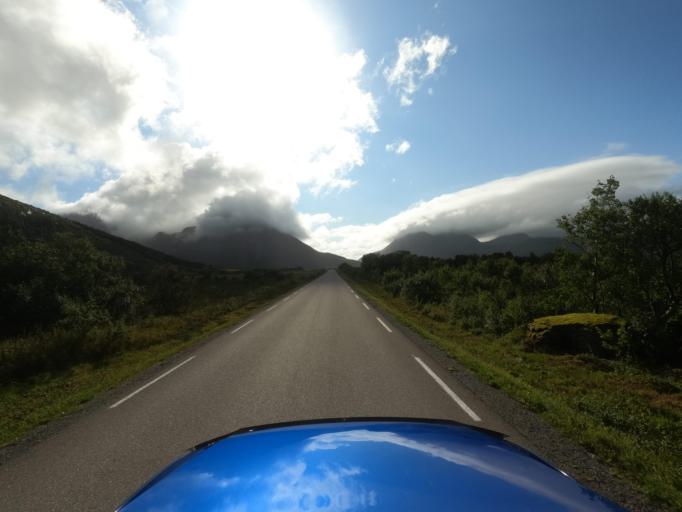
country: NO
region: Nordland
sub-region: Vagan
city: Kabelvag
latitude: 68.3003
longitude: 14.1678
